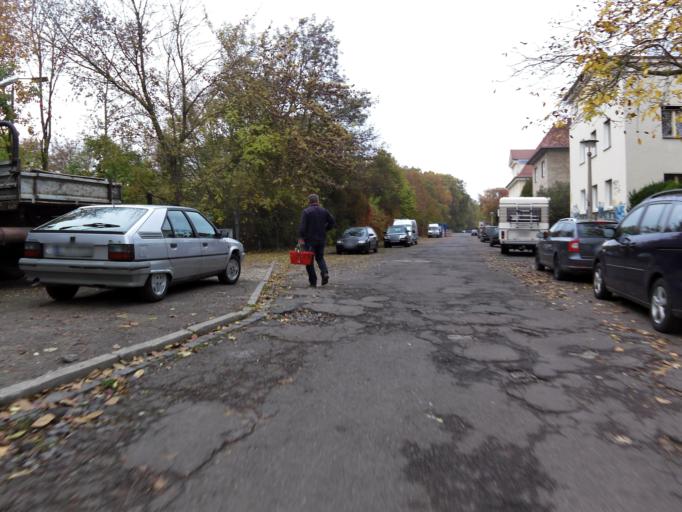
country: DE
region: Saxony
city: Leipzig
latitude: 51.3126
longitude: 12.3659
